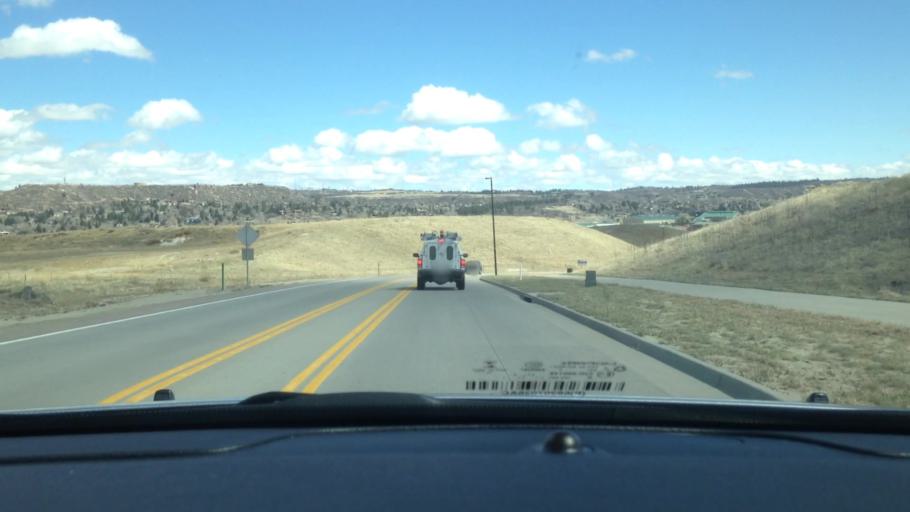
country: US
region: Colorado
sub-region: Douglas County
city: Castle Rock
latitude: 39.3693
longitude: -104.8742
